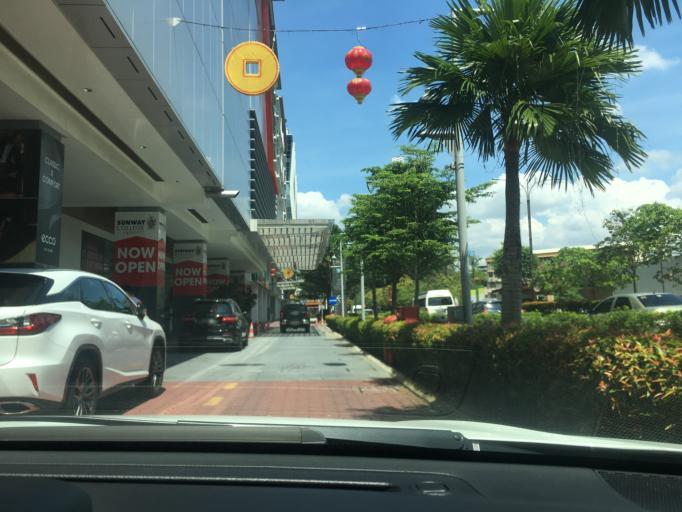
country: MY
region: Kuala Lumpur
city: Kuala Lumpur
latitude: 3.1281
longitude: 101.7246
